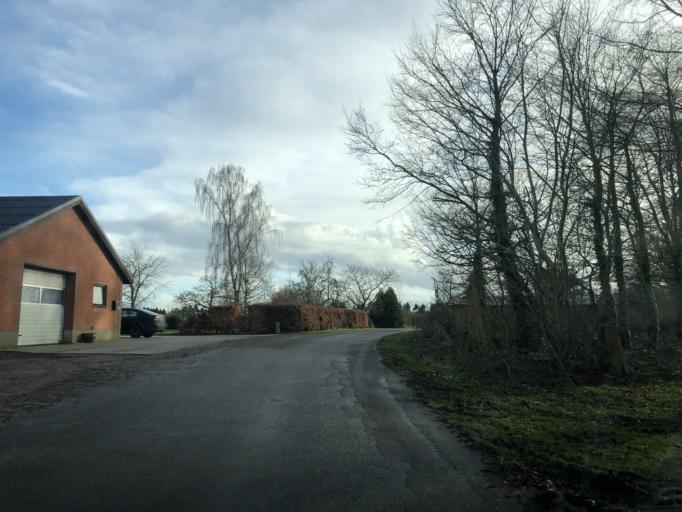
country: DK
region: Central Jutland
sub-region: Viborg Kommune
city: Viborg
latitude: 56.5106
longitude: 9.4275
